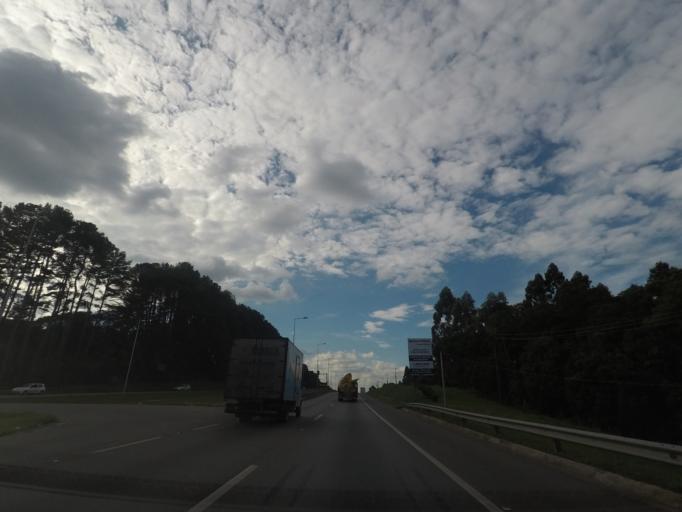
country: BR
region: Parana
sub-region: Araucaria
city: Araucaria
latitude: -25.5758
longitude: -49.3120
